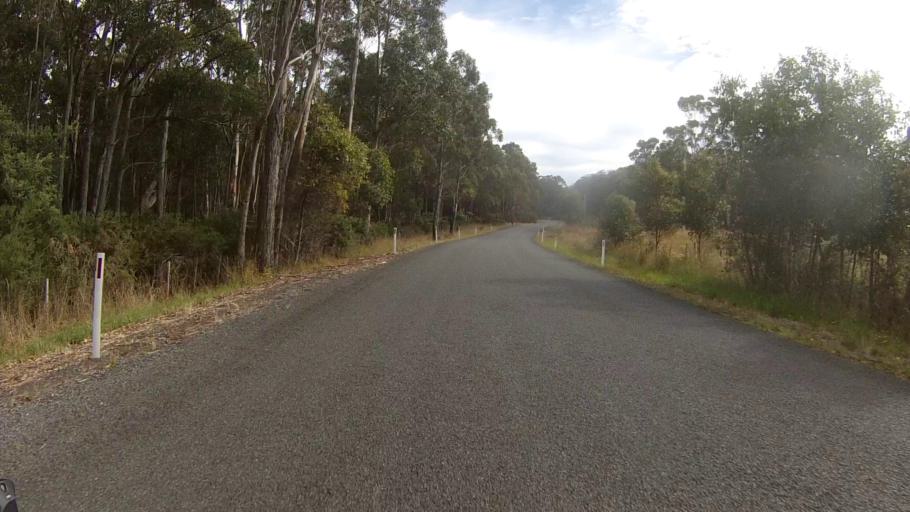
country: AU
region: Tasmania
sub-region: Sorell
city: Sorell
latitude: -42.8164
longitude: 147.7913
